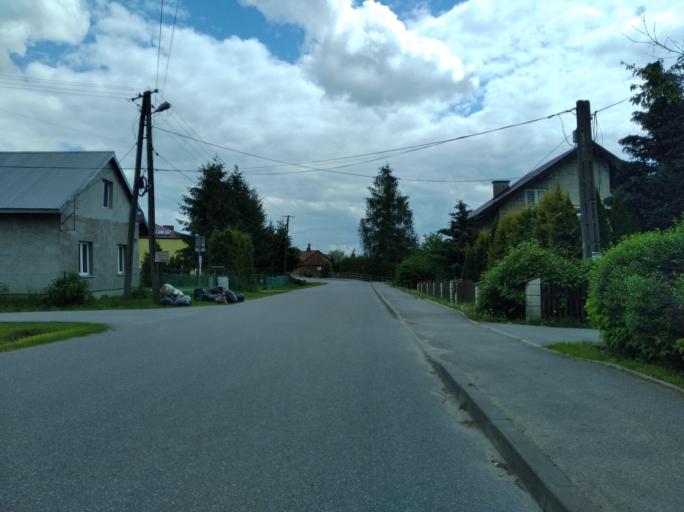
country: PL
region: Subcarpathian Voivodeship
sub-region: Powiat brzozowski
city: Jasionow
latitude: 49.6585
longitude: 21.9816
